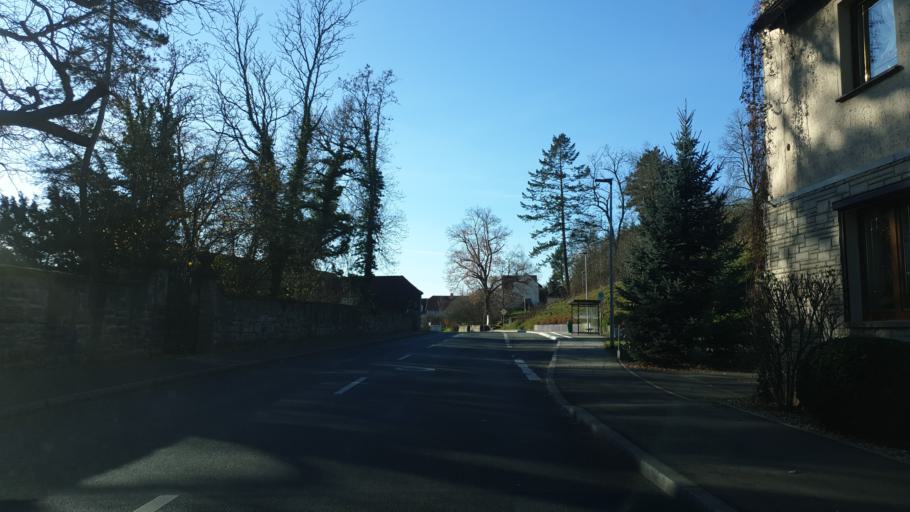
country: DE
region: Thuringia
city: Hartmannsdorf
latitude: 50.9616
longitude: 11.9772
